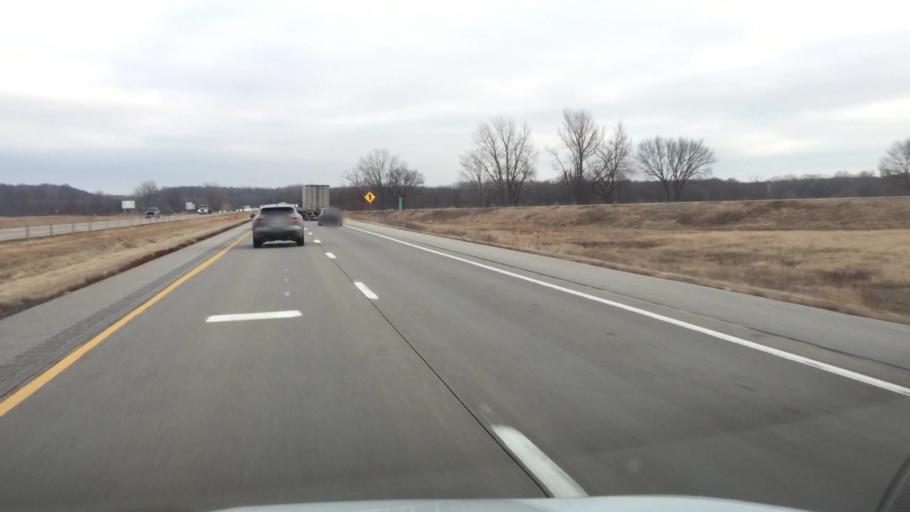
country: US
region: Iowa
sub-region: Jasper County
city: Colfax
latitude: 41.6902
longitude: -93.1792
